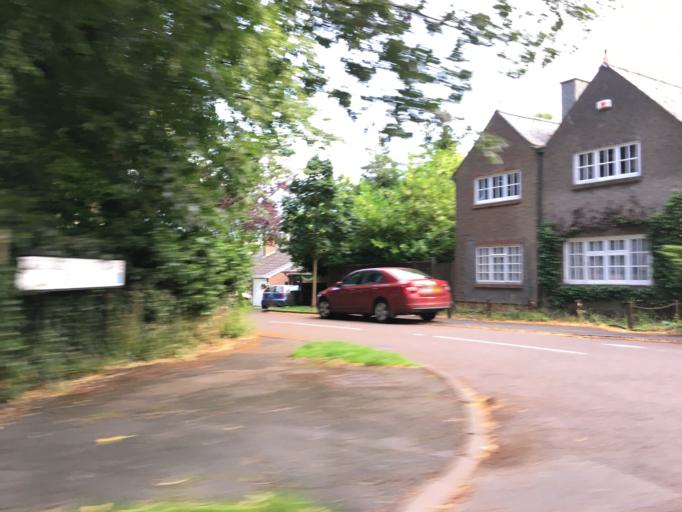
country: GB
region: England
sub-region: Warwickshire
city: Rugby
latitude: 52.3603
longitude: -1.2731
